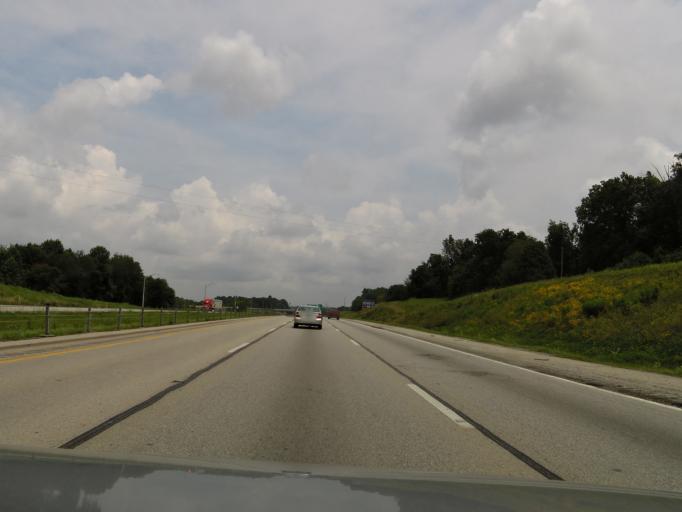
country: US
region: Kentucky
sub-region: Hardin County
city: Elizabethtown
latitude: 37.6959
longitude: -85.8380
